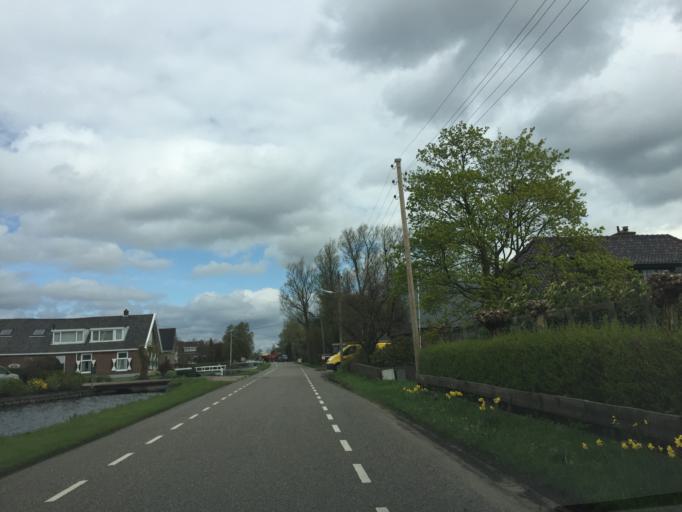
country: NL
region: South Holland
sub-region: Gemeente Waddinxveen
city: Vondelwijk
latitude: 52.0592
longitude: 4.6706
